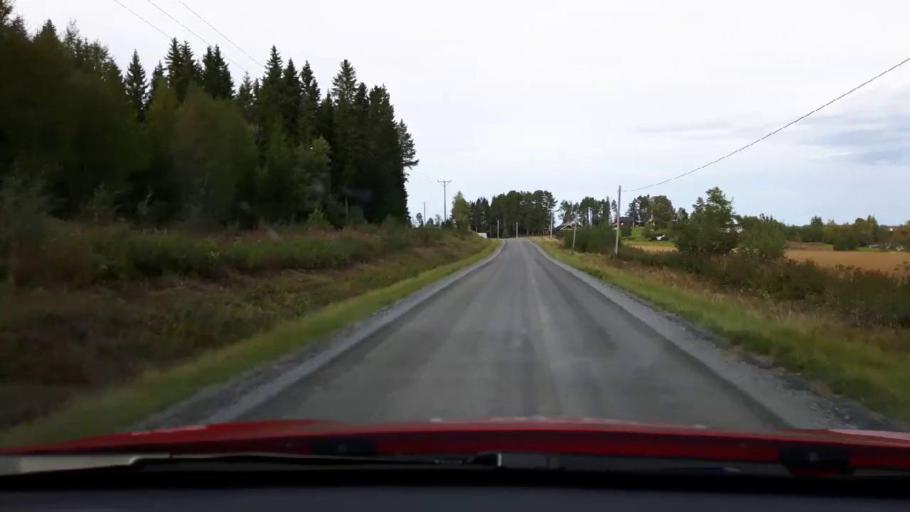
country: SE
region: Jaemtland
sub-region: Krokoms Kommun
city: Valla
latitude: 63.2541
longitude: 13.9487
